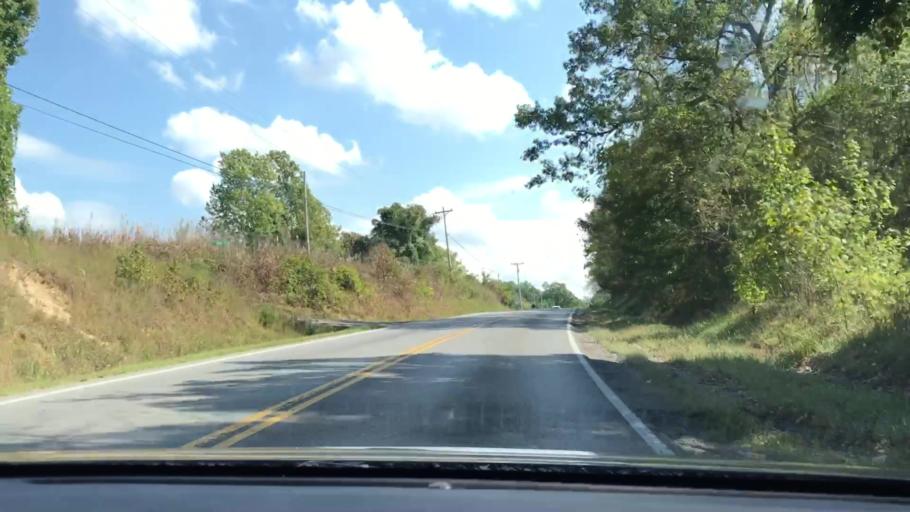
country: US
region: Kentucky
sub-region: Trigg County
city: Cadiz
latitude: 36.8111
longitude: -87.8984
